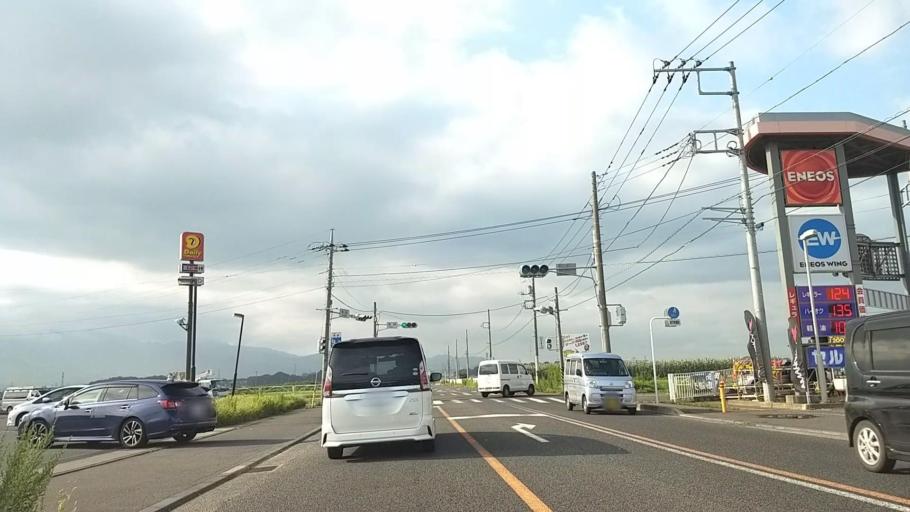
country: JP
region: Kanagawa
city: Isehara
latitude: 35.3645
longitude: 139.3238
